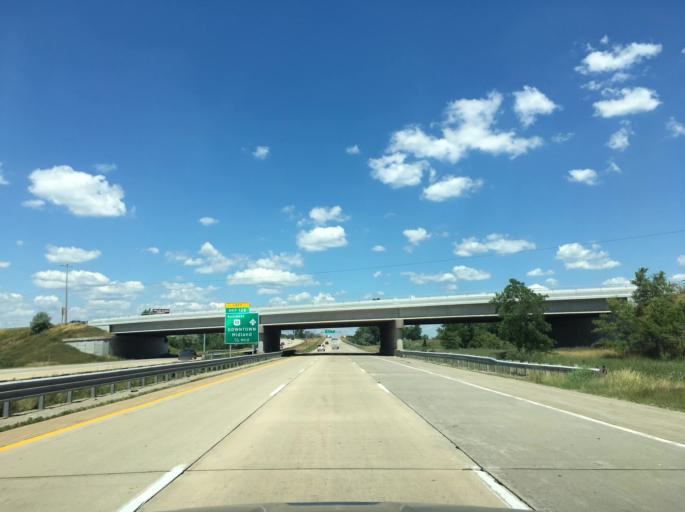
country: US
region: Michigan
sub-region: Saginaw County
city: Freeland
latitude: 43.6040
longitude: -84.1601
